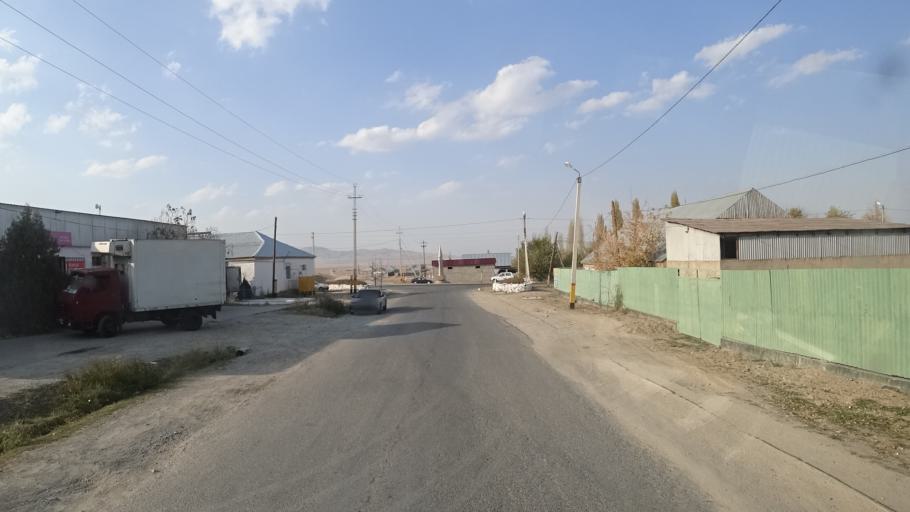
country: KZ
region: Zhambyl
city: Taraz
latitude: 42.8362
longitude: 71.2096
